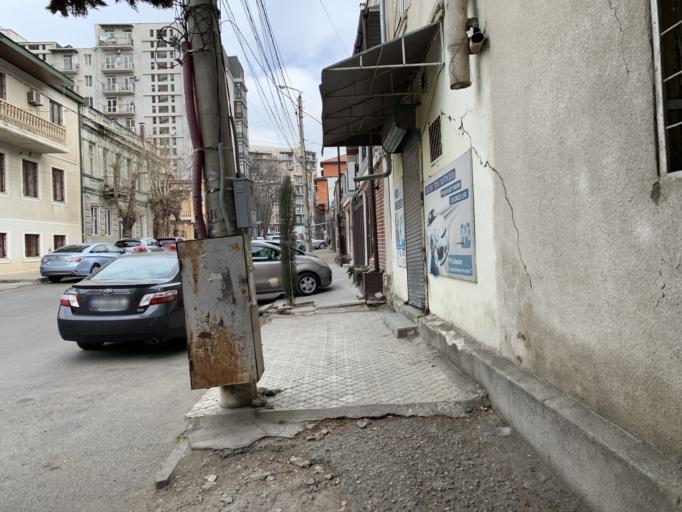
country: GE
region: T'bilisi
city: Tbilisi
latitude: 41.6799
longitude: 44.8389
